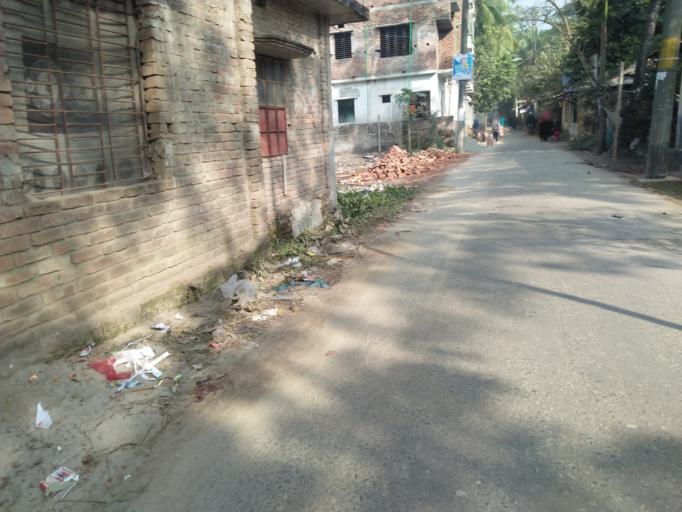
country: BD
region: Barisal
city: Bhola
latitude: 22.6793
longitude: 90.6424
